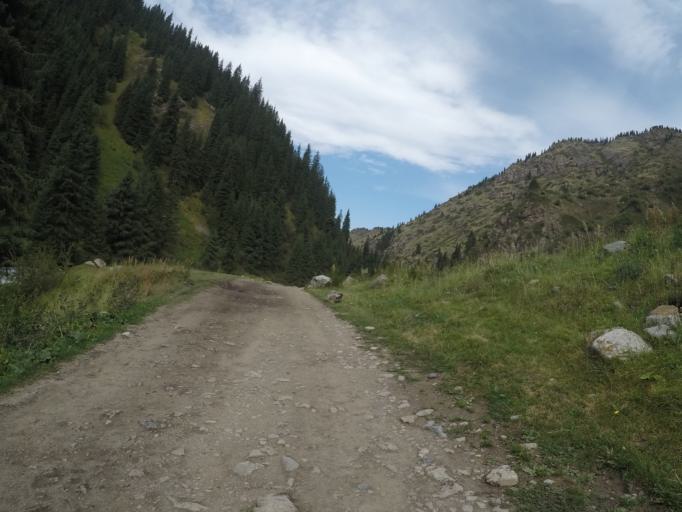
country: KG
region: Ysyk-Koel
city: Teploklyuchenka
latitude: 42.4389
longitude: 78.5587
